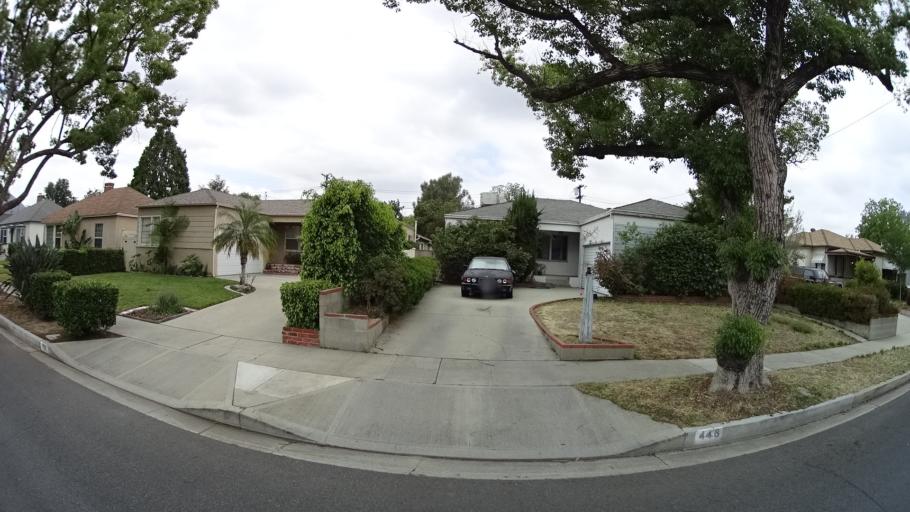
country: US
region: California
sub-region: Los Angeles County
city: Burbank
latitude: 34.1659
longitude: -118.3343
